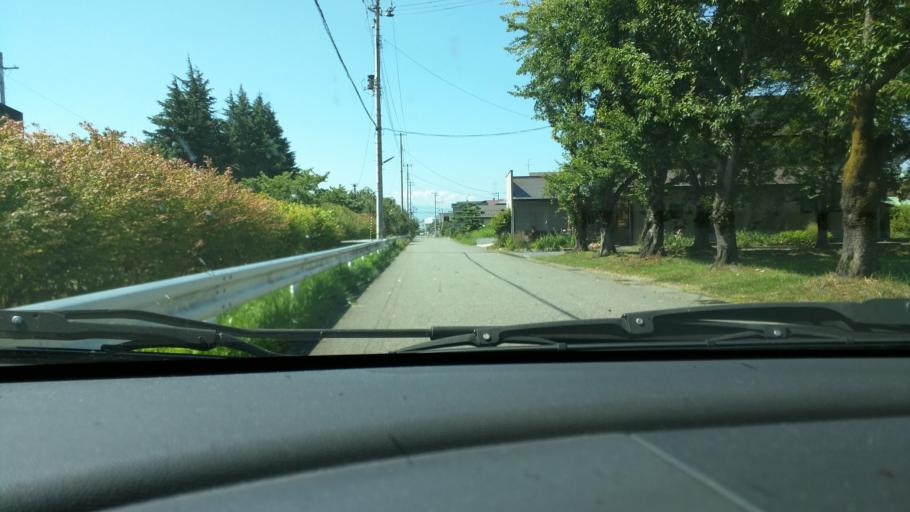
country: JP
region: Fukushima
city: Kitakata
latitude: 37.6553
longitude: 139.8662
